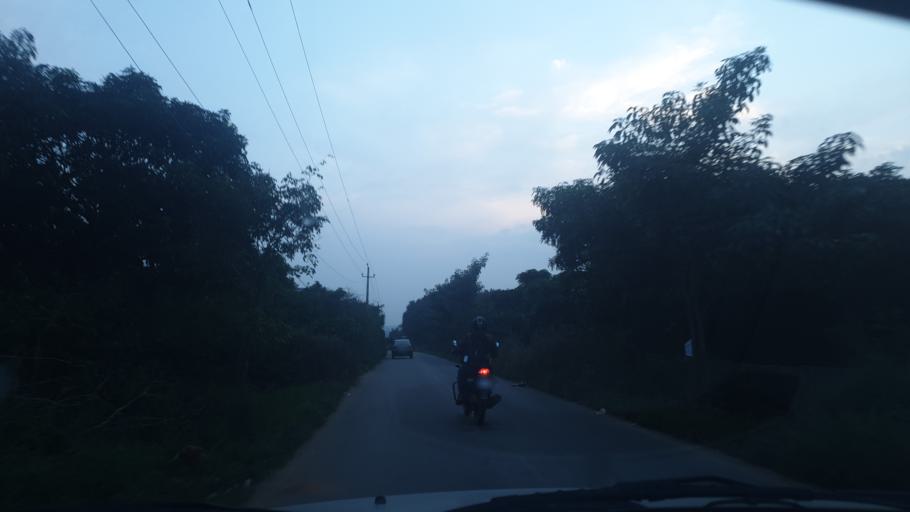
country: IN
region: Karnataka
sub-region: Bangalore Urban
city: Yelahanka
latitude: 13.0584
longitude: 77.6845
